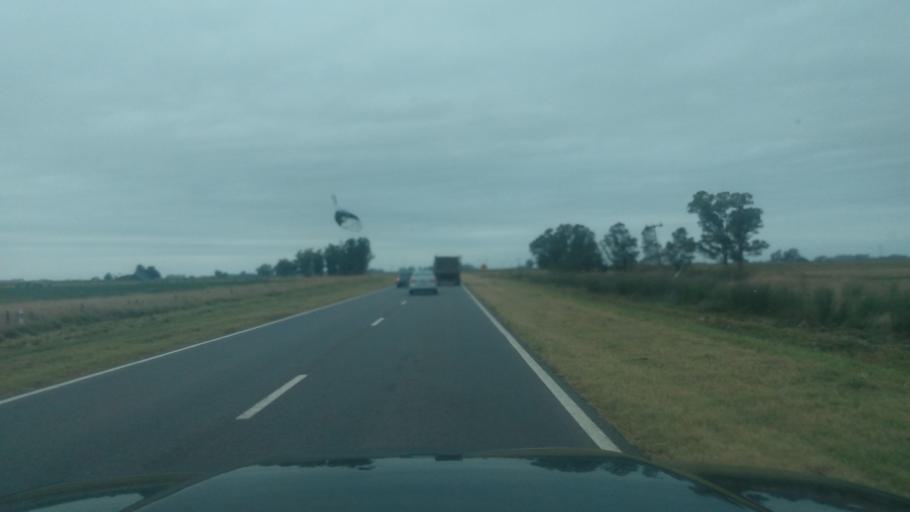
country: AR
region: Buenos Aires
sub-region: Partido de Nueve de Julio
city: Nueve de Julio
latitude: -35.3980
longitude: -60.7514
